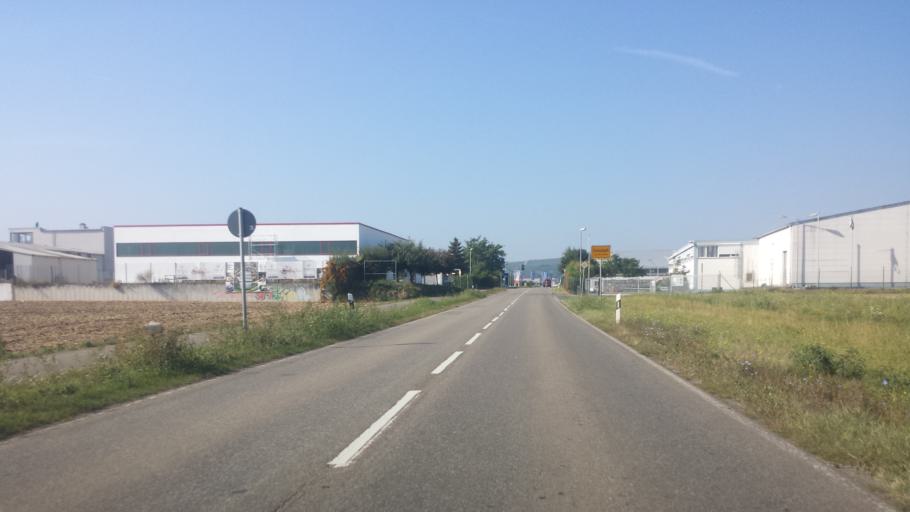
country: DE
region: Rheinland-Pfalz
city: Heidesheim
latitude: 49.5635
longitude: 8.1850
